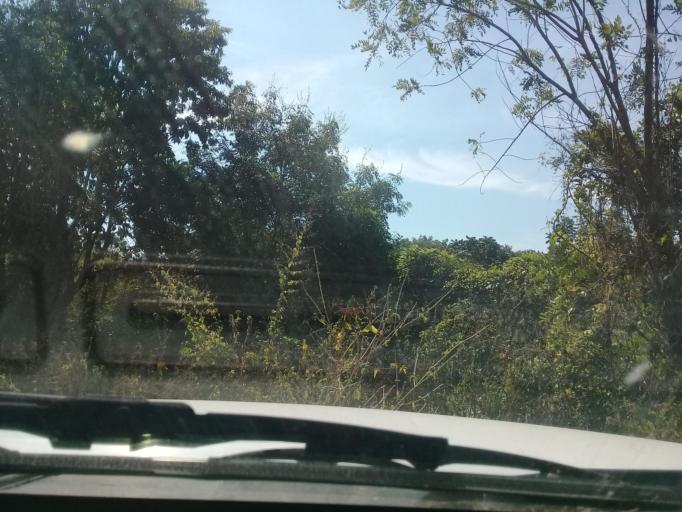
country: MX
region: Veracruz
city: Rinconada
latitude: 19.4387
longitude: -96.5644
